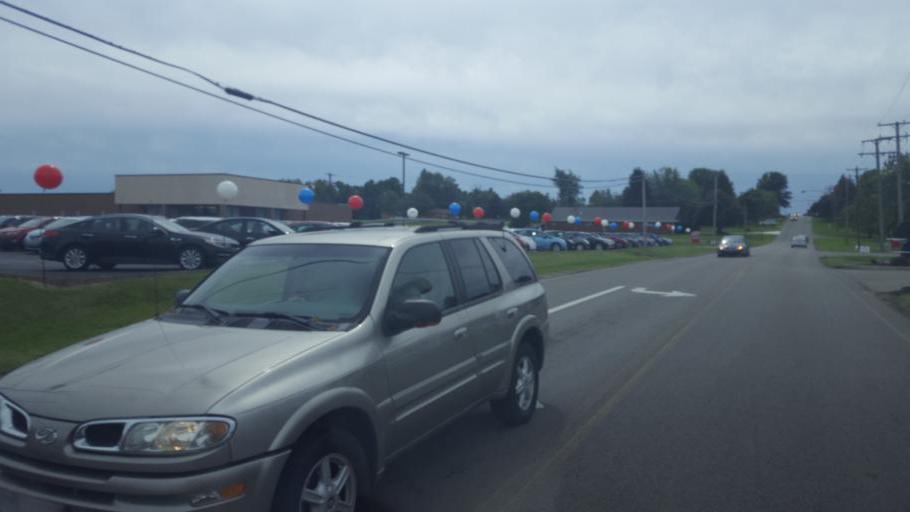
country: US
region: Ohio
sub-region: Richland County
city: Ontario
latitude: 40.7678
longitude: -82.5634
